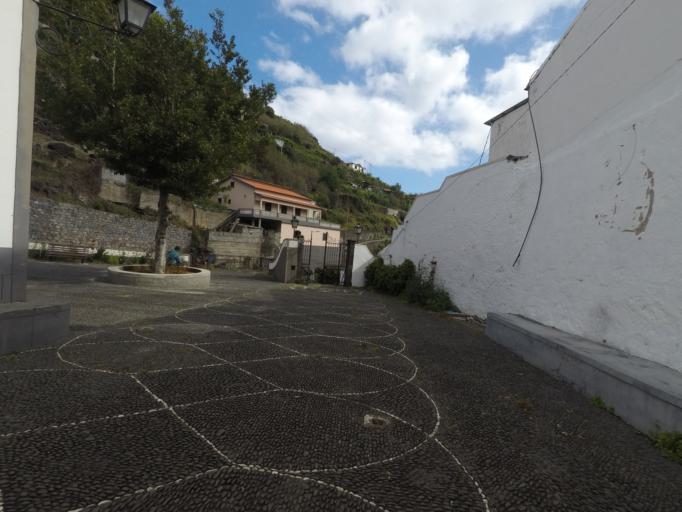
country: PT
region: Madeira
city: Calheta
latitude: 32.7231
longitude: -17.1772
